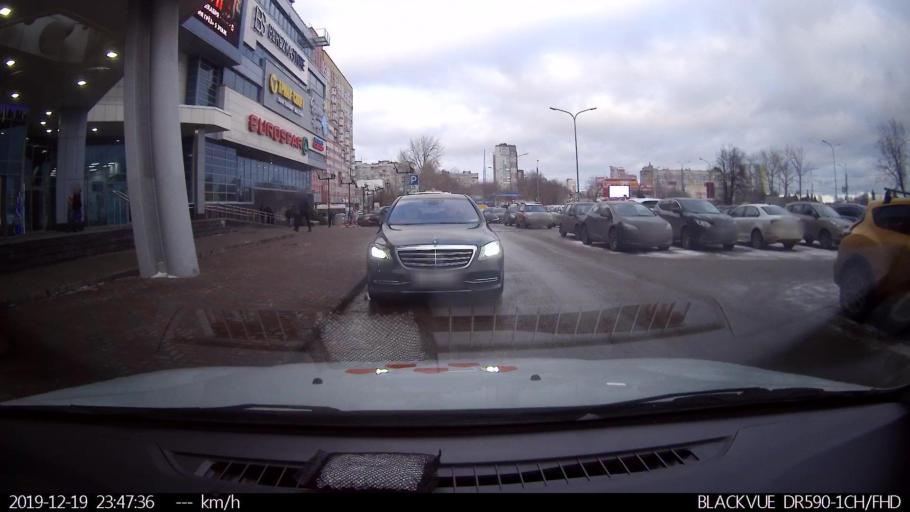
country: RU
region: Tverskaya
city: Ves'yegonsk
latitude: 58.7081
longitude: 37.5715
